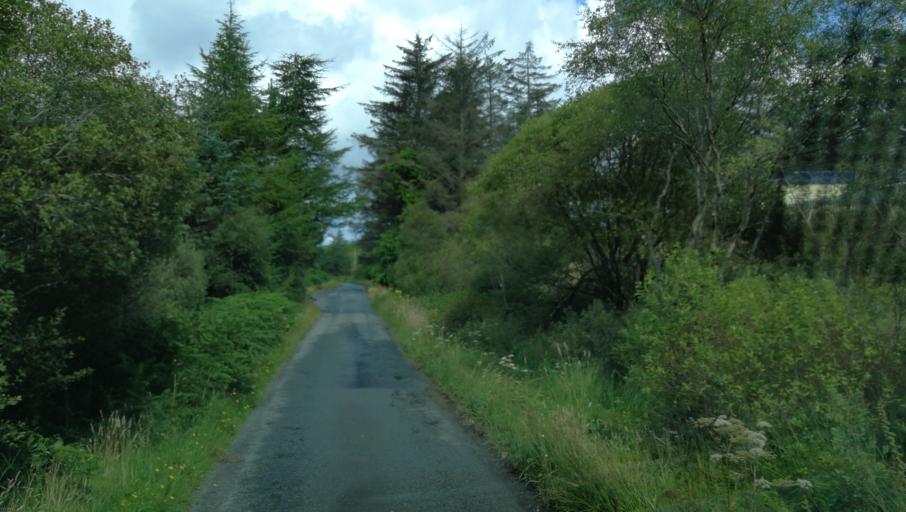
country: GB
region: Scotland
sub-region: Highland
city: Portree
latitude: 57.3801
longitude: -6.1950
